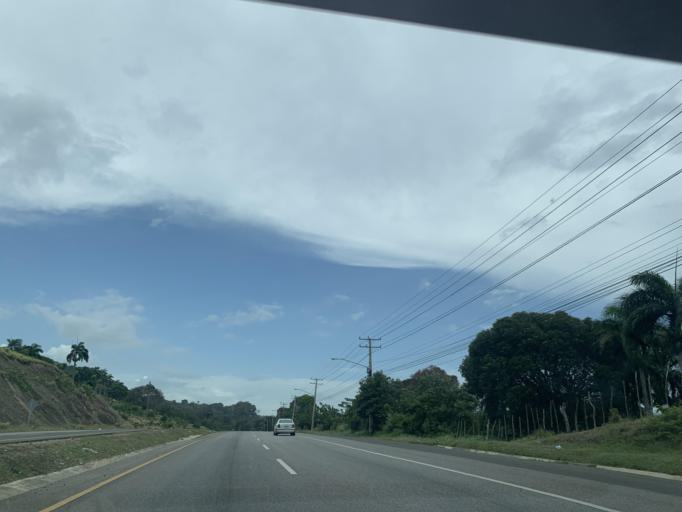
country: DO
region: Puerto Plata
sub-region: Puerto Plata
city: Puerto Plata
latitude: 19.8278
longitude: -70.7528
